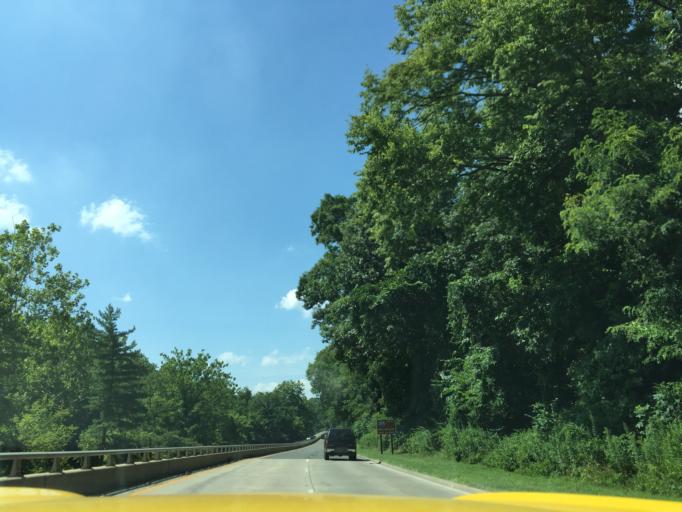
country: US
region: Maryland
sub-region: Montgomery County
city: Cabin John
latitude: 38.9660
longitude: -77.1403
